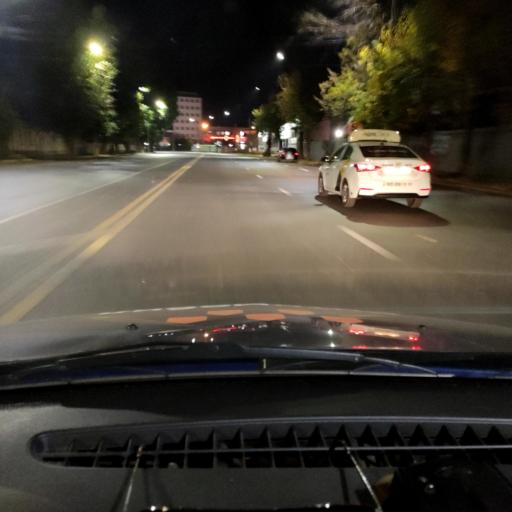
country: RU
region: Voronezj
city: Voronezh
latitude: 51.6803
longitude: 39.1782
